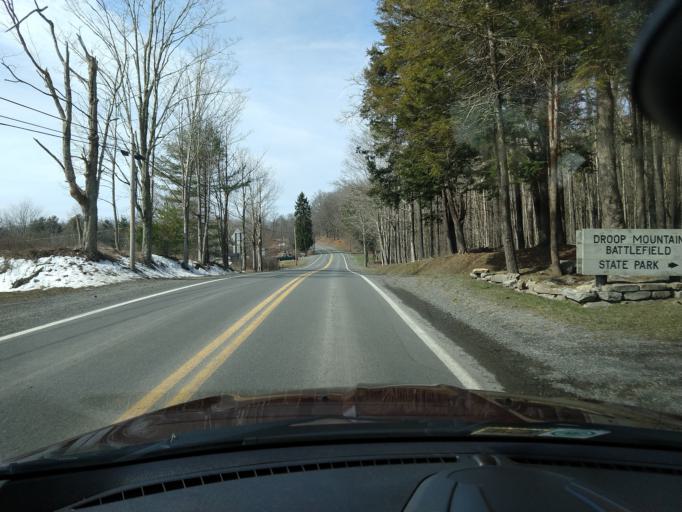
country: US
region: West Virginia
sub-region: Pocahontas County
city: Marlinton
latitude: 38.1107
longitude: -80.2659
